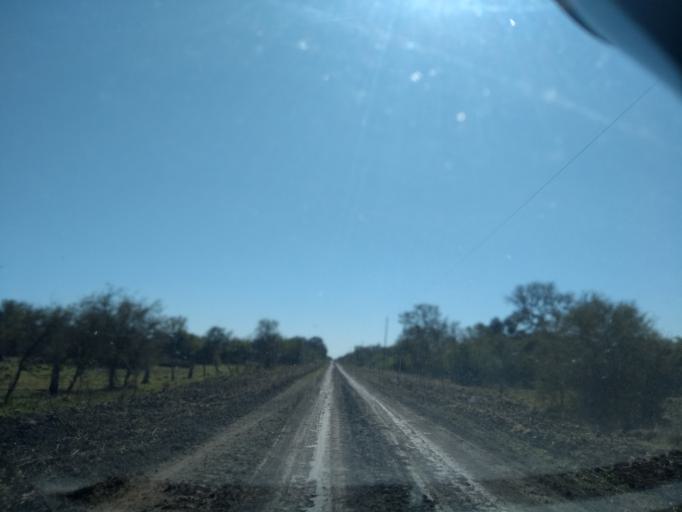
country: AR
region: Chaco
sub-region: Departamento de Quitilipi
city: Quitilipi
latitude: -26.7528
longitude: -60.2415
